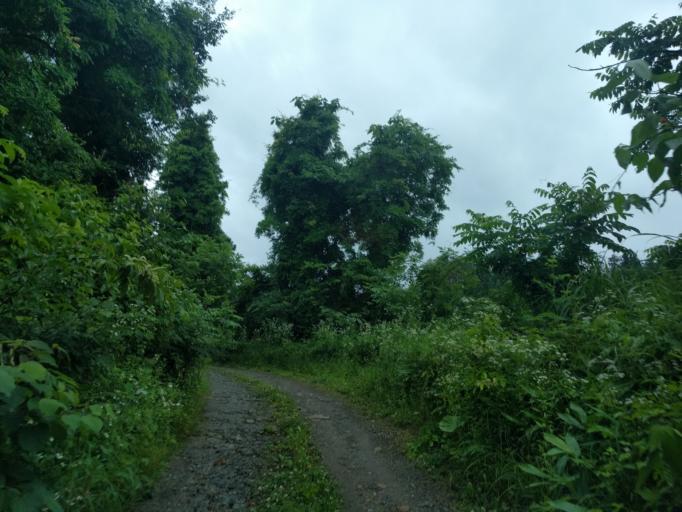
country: JP
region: Fukushima
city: Kitakata
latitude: 37.5151
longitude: 139.8012
